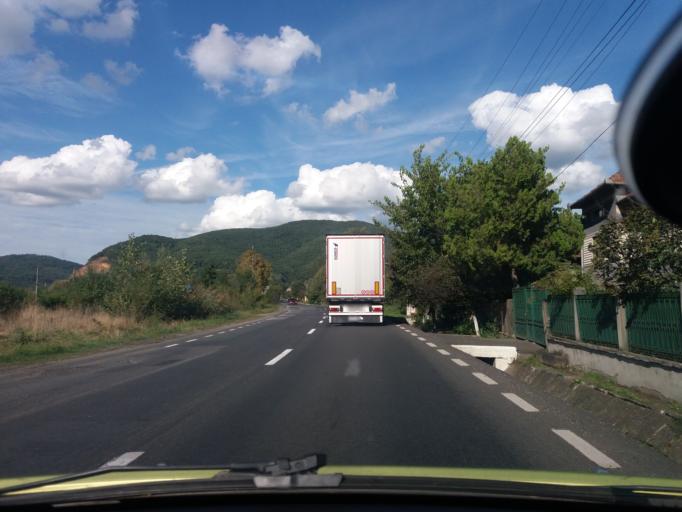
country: RO
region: Hunedoara
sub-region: Comuna Zam
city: Zam
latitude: 45.9977
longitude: 22.4393
